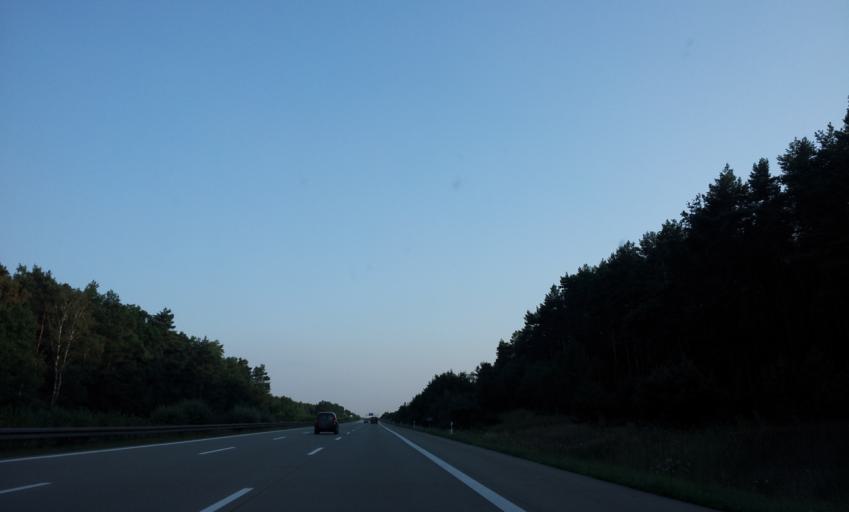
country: DE
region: Brandenburg
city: Erkner
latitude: 52.3593
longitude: 13.7601
